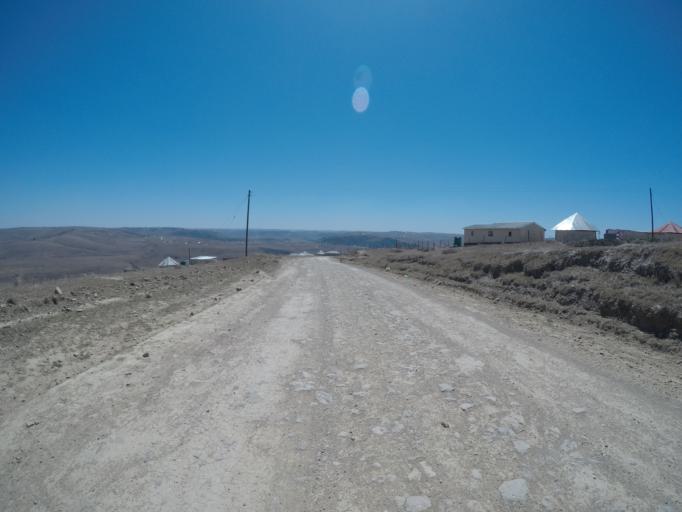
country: ZA
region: Eastern Cape
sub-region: OR Tambo District Municipality
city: Mthatha
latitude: -31.8892
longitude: 28.8771
